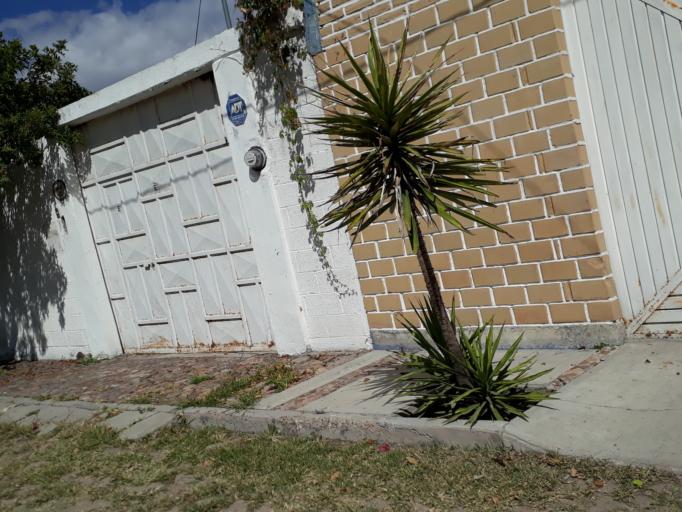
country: MX
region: Aguascalientes
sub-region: Aguascalientes
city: San Sebastian [Fraccionamiento]
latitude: 21.7926
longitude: -102.2793
